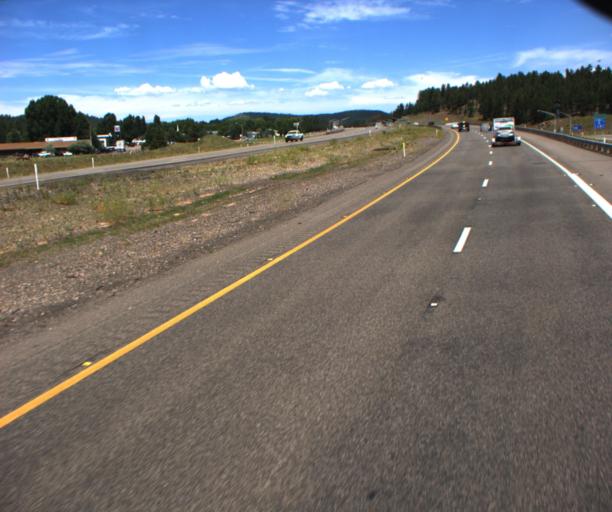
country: US
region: Arizona
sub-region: Coconino County
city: Sedona
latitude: 34.9400
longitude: -111.6511
